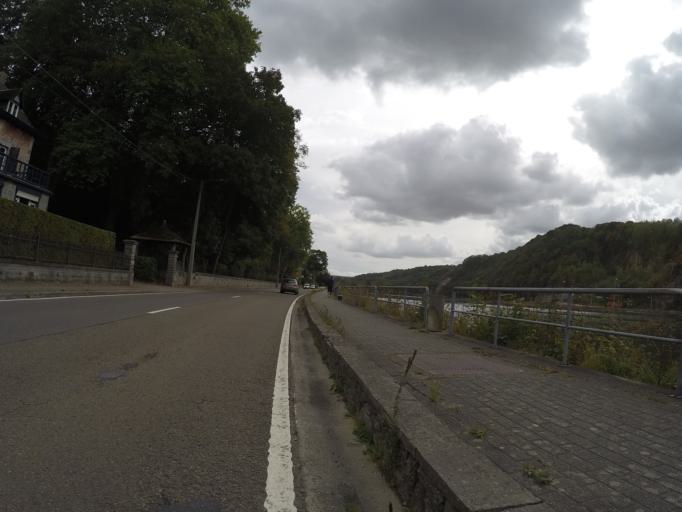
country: BE
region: Wallonia
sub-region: Province de Namur
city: Yvoir
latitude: 50.3352
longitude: 4.8738
